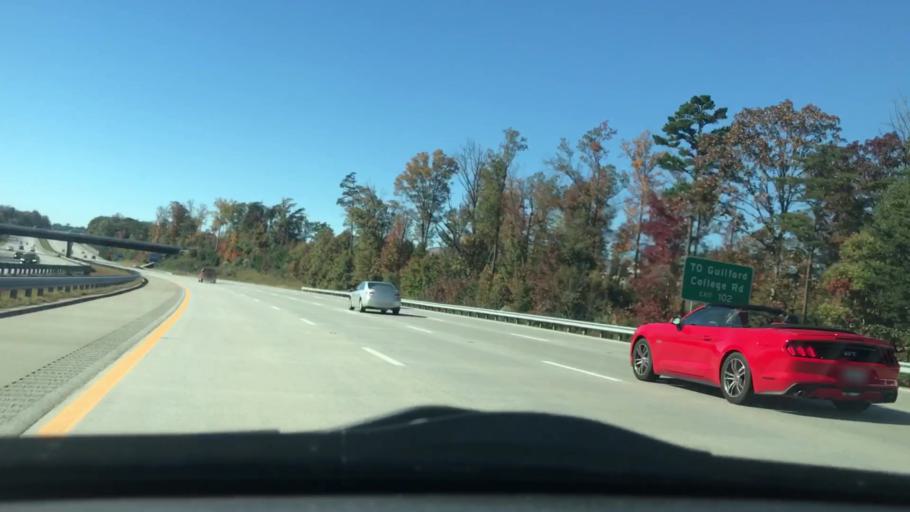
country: US
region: North Carolina
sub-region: Guilford County
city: Jamestown
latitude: 36.0448
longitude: -79.8987
